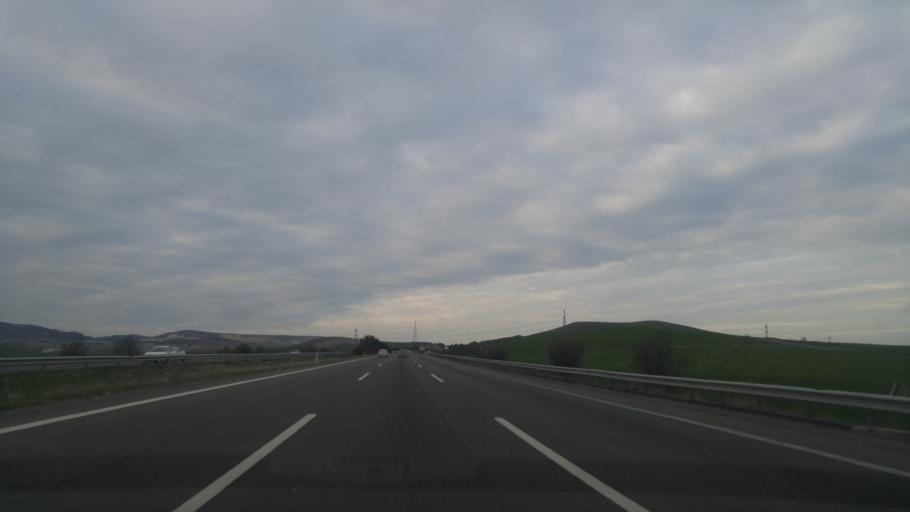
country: TR
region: Ankara
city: Kazan
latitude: 40.1392
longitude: 32.5986
